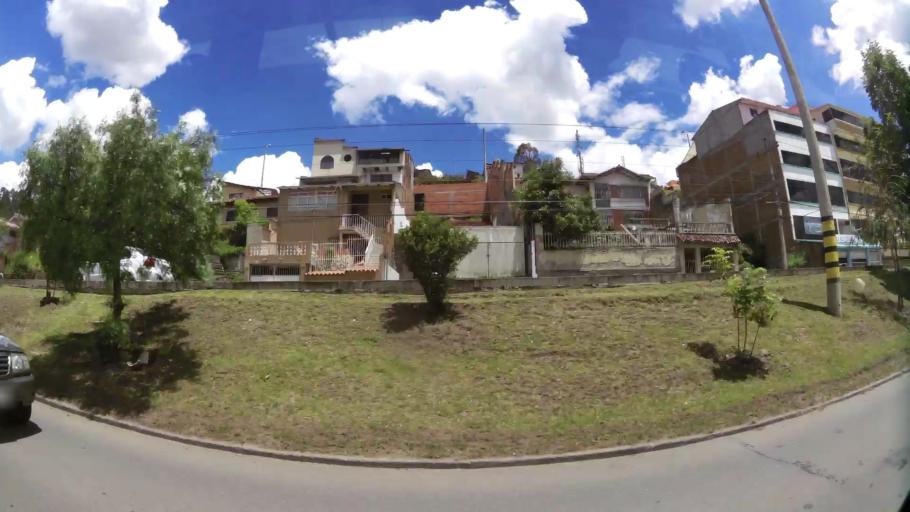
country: EC
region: Azuay
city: Cuenca
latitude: -2.8889
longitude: -79.0148
